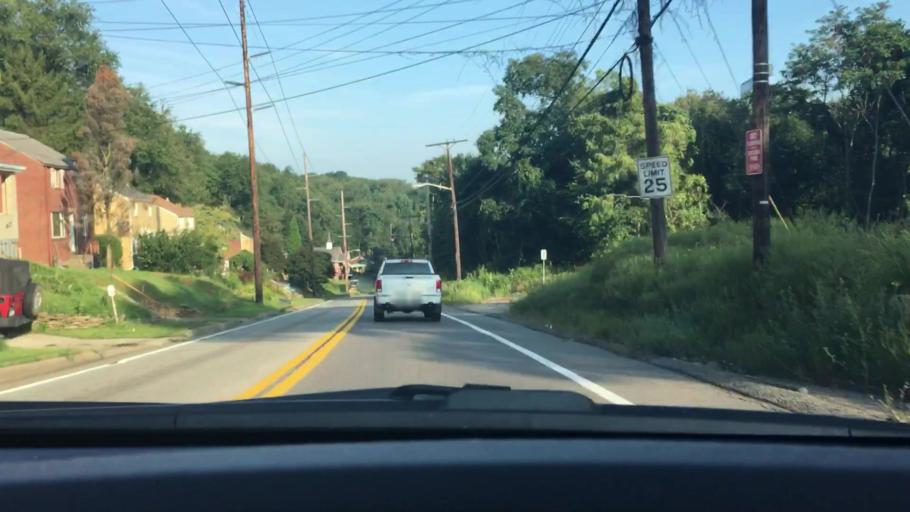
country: US
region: Pennsylvania
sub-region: Allegheny County
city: West Homestead
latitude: 40.3713
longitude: -79.9153
